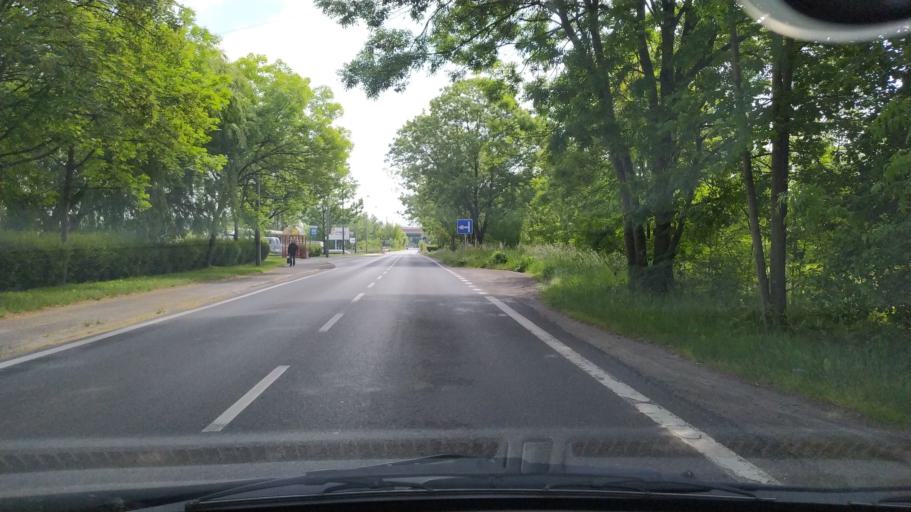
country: PL
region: Silesian Voivodeship
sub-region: Gliwice
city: Gliwice
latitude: 50.2901
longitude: 18.7101
